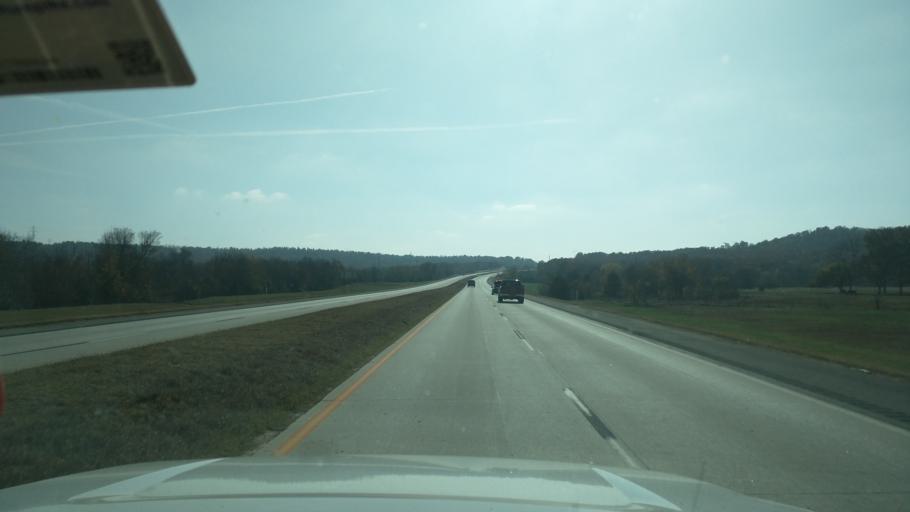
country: US
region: Oklahoma
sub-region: Muskogee County
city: Muskogee
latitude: 35.6721
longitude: -95.3091
